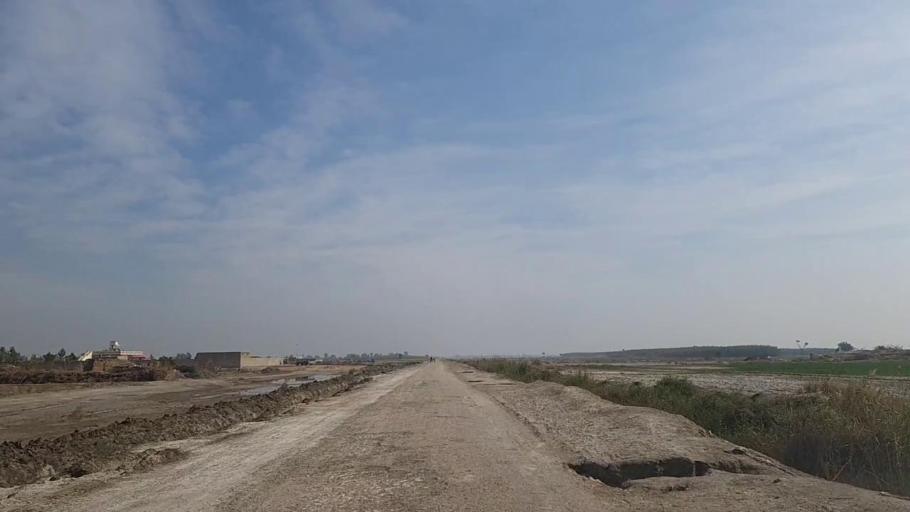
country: PK
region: Sindh
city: Nawabshah
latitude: 26.3319
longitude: 68.4528
